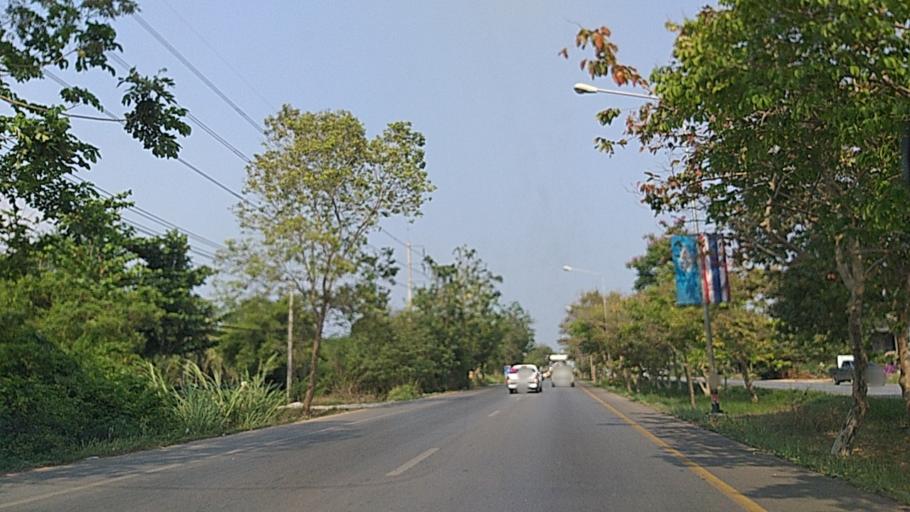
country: TH
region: Chanthaburi
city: Na Yai Am
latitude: 12.7828
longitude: 101.7400
